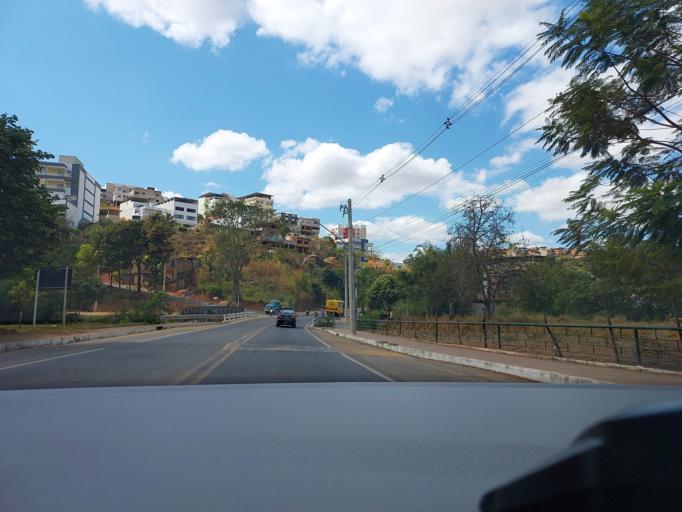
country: BR
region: Minas Gerais
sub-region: Muriae
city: Muriae
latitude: -21.1257
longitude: -42.3553
